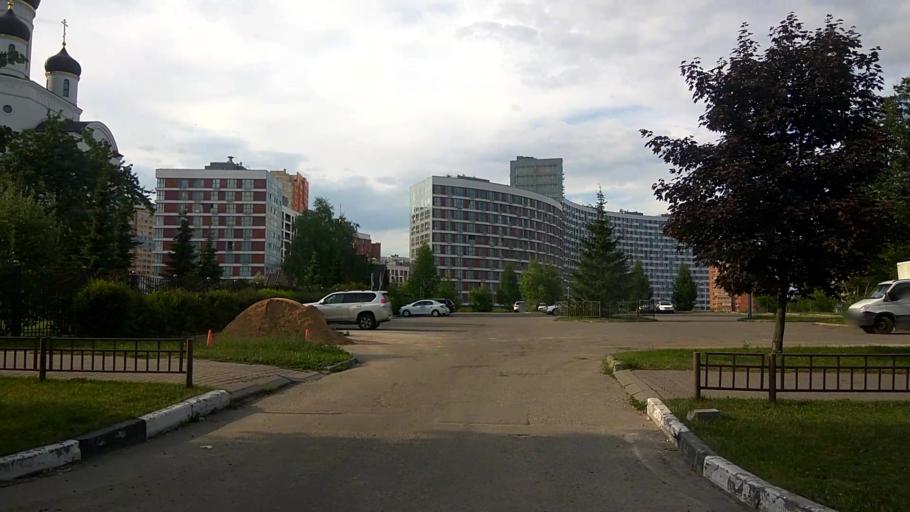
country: RU
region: Moskovskaya
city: Mytishchi
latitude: 55.9161
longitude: 37.7490
